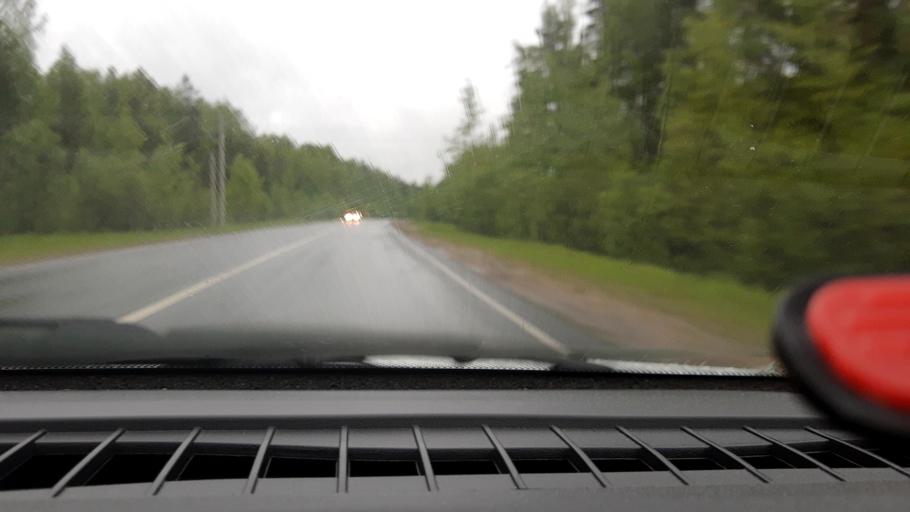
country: RU
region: Nizjnij Novgorod
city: Semenov
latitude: 56.8058
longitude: 44.4631
